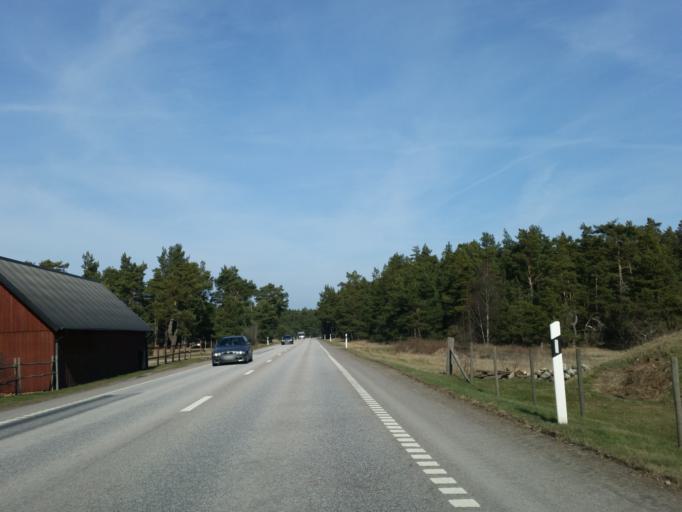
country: SE
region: Kalmar
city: Faerjestaden
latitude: 56.7453
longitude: 16.5475
